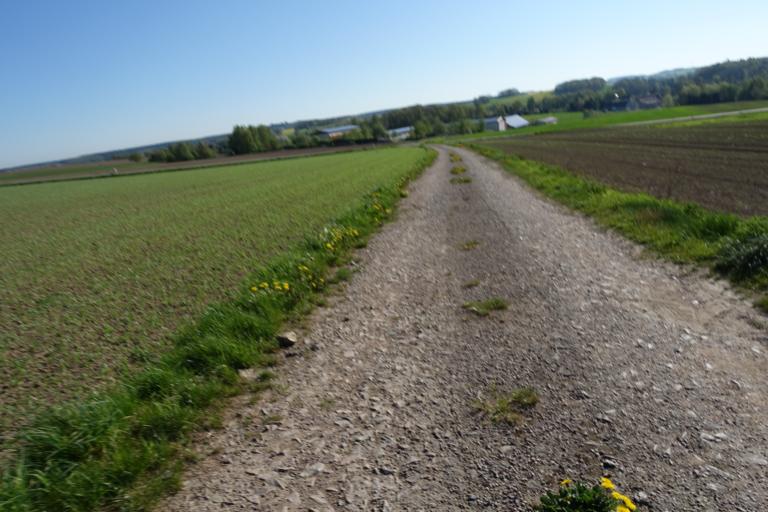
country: DE
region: Saxony
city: Niederschona
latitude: 50.9013
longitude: 13.4247
